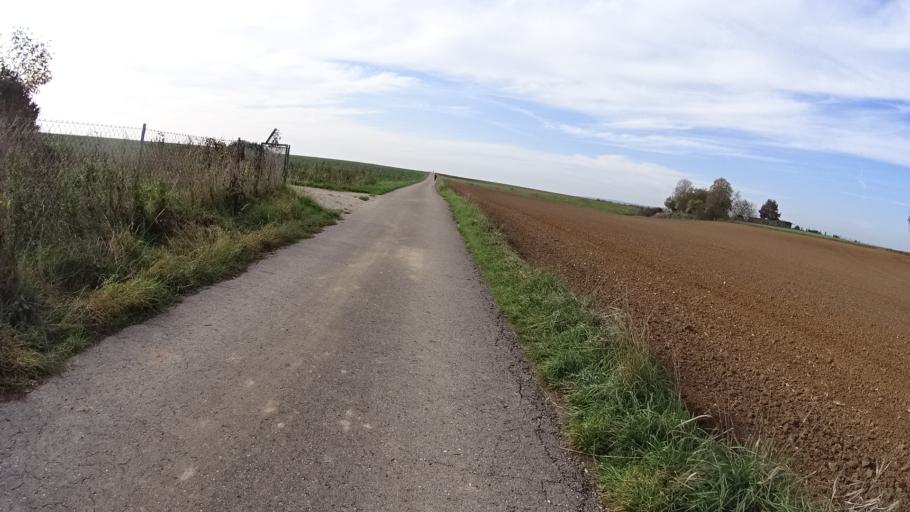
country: DE
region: Bavaria
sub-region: Upper Bavaria
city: Eitensheim
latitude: 48.8192
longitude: 11.3132
